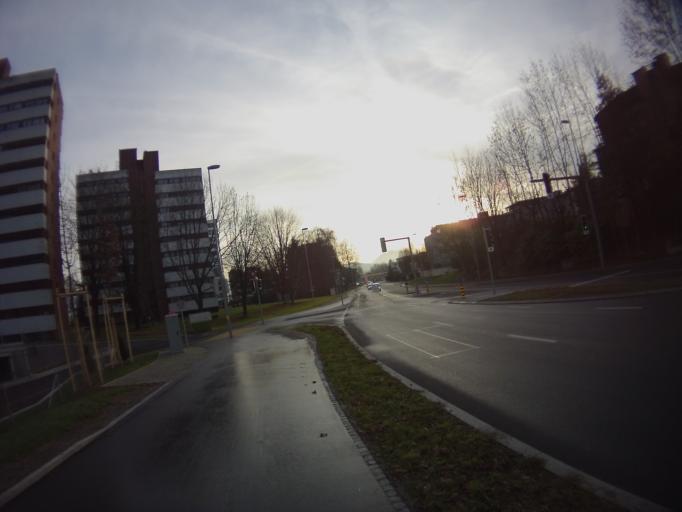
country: CH
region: Zug
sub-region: Zug
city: Cham
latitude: 47.1850
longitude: 8.4741
